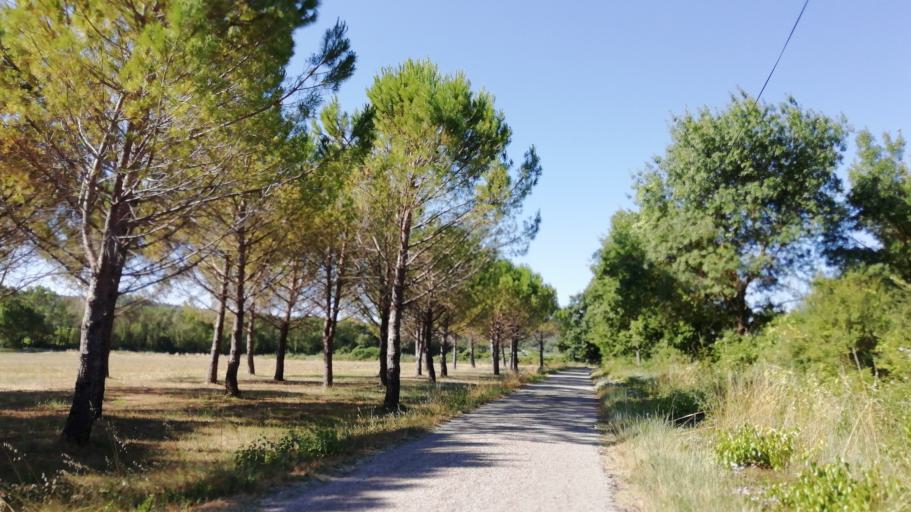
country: FR
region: Languedoc-Roussillon
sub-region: Departement de l'Herault
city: Saint-Martin-de-Londres
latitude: 43.7901
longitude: 3.7475
